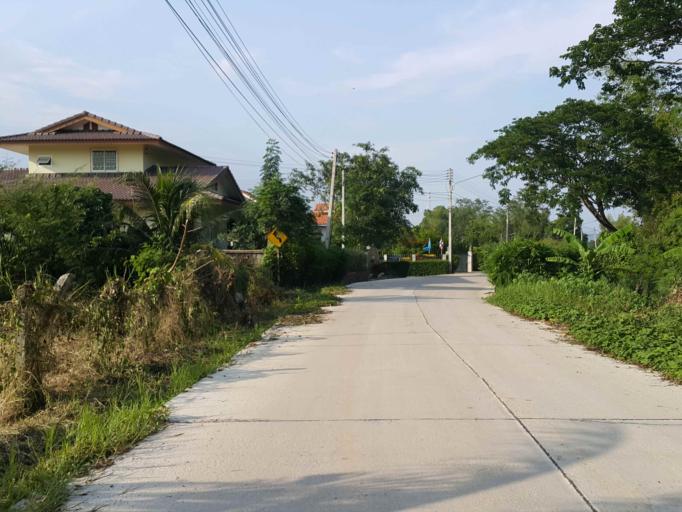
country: TH
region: Chiang Mai
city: San Sai
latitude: 18.8376
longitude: 99.0920
